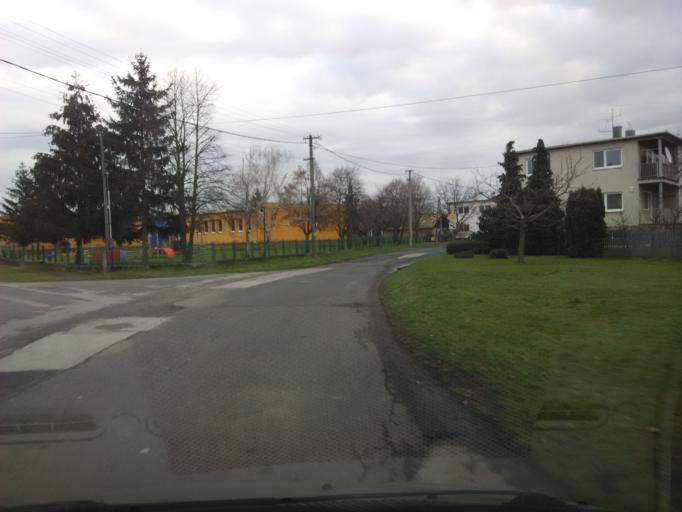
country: SK
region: Nitriansky
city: Tlmace
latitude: 48.2428
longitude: 18.5334
